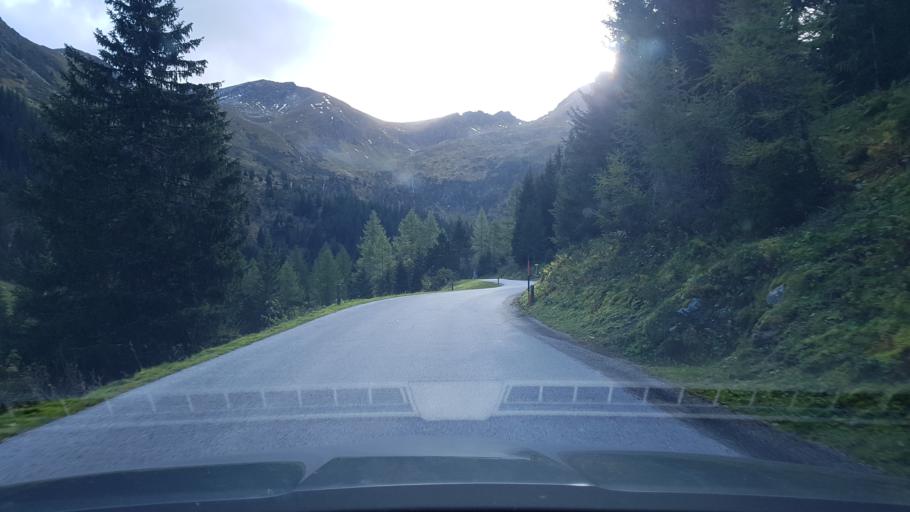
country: AT
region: Styria
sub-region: Politischer Bezirk Liezen
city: Sankt Nikolai im Solktal
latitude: 47.2801
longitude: 14.0883
